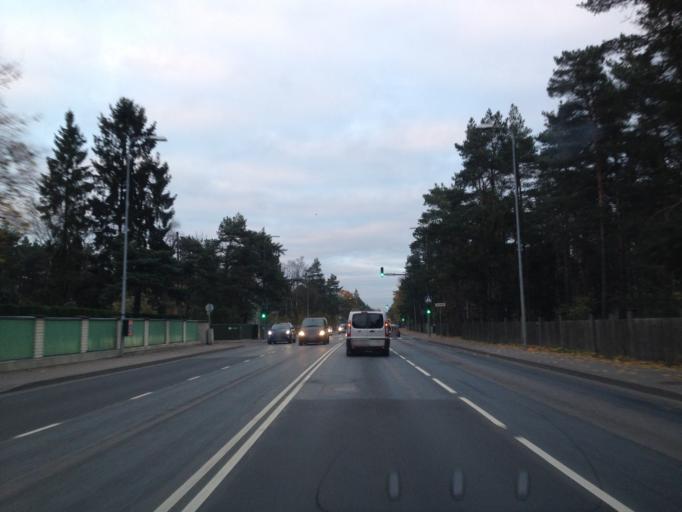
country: EE
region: Harju
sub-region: Saue vald
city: Laagri
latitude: 59.3691
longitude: 24.6550
